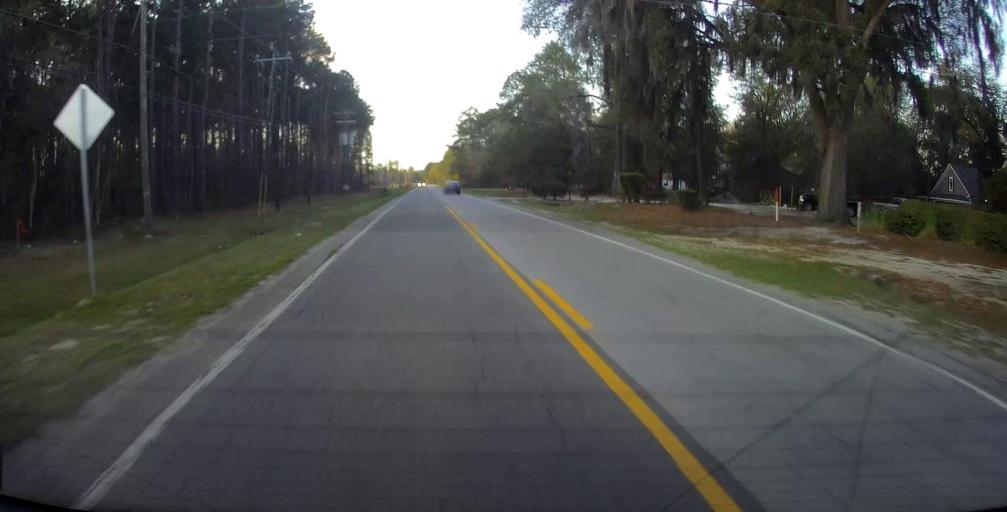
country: US
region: Georgia
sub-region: Chatham County
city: Bloomingdale
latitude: 32.1354
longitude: -81.3890
